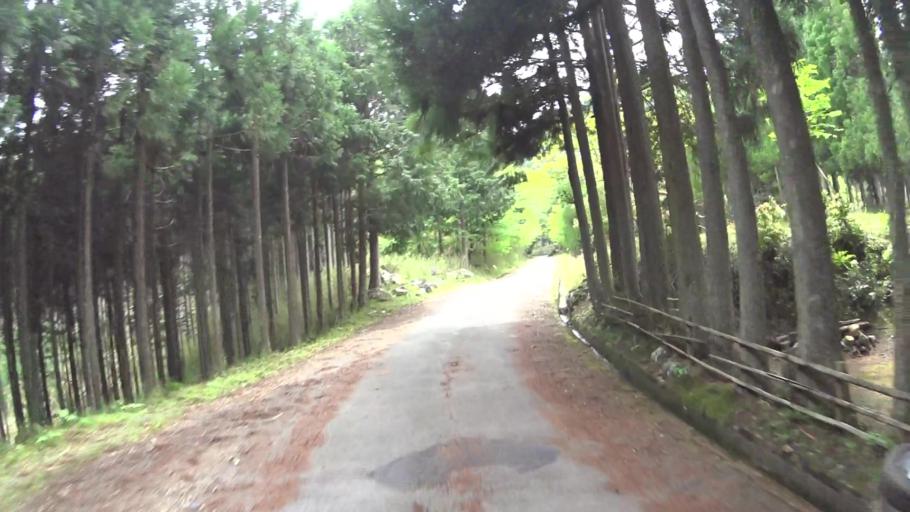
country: JP
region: Kyoto
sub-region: Kyoto-shi
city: Kamigyo-ku
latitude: 35.1965
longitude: 135.7028
